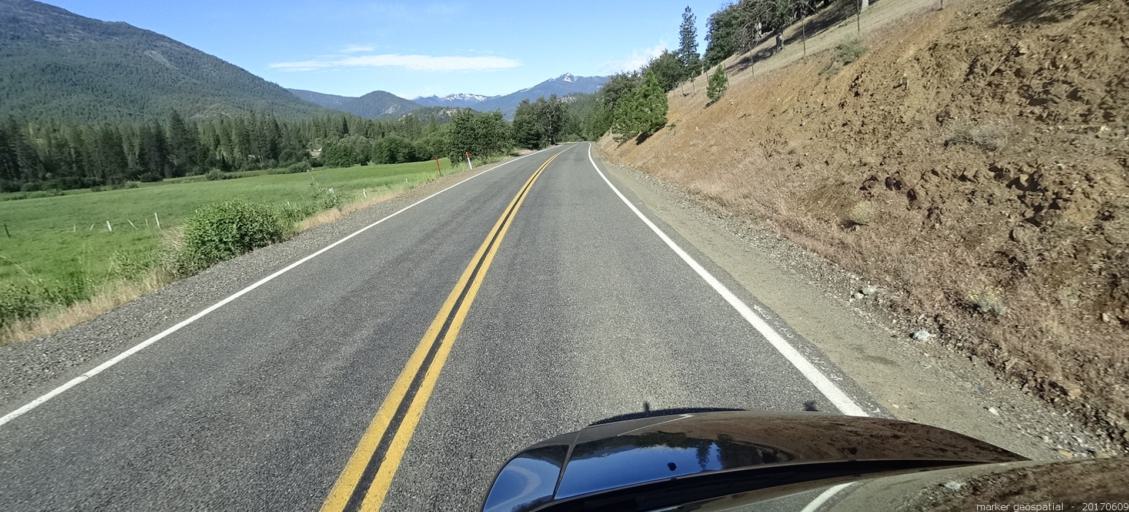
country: US
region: California
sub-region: Siskiyou County
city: Weed
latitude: 41.3124
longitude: -122.7562
